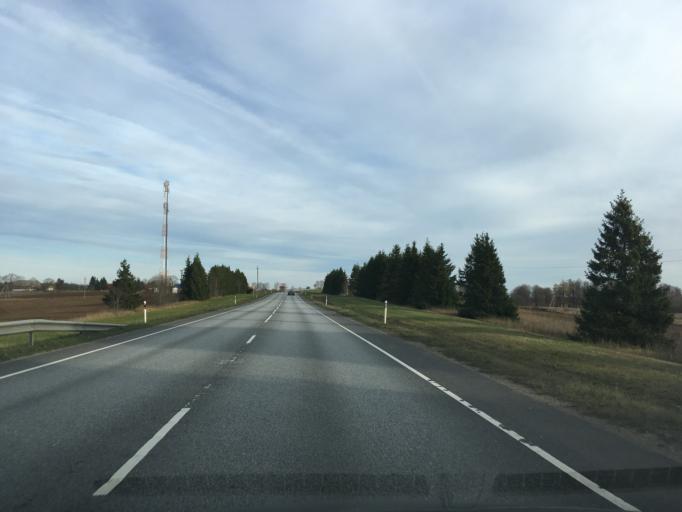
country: EE
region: Ida-Virumaa
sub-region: Narva-Joesuu linn
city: Narva-Joesuu
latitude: 59.3857
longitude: 27.9725
